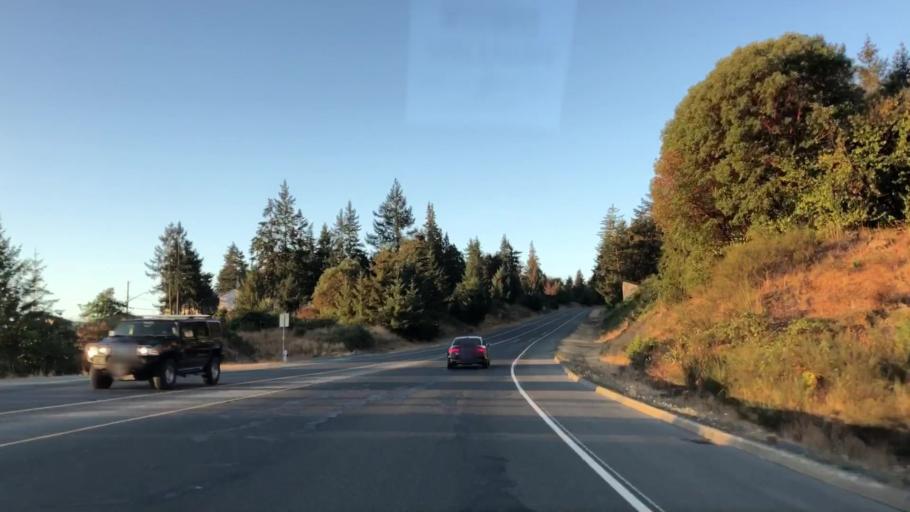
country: CA
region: British Columbia
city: Colwood
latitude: 48.4264
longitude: -123.5019
